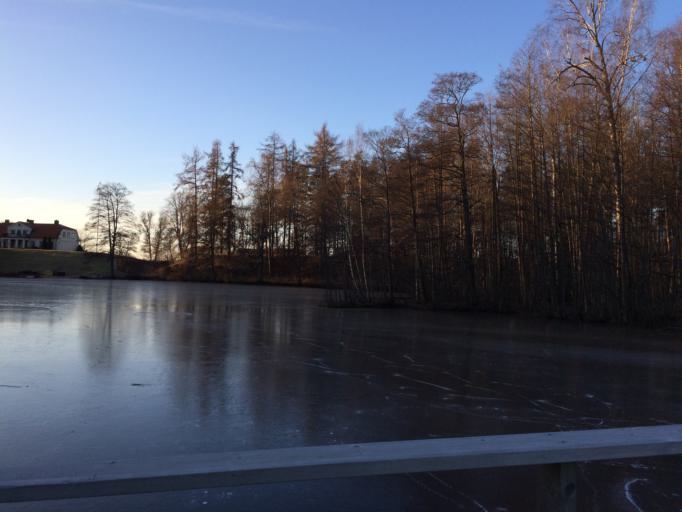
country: SE
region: Vaestmanland
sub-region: Hallstahammars Kommun
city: Hallstahammar
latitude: 59.6120
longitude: 16.2073
